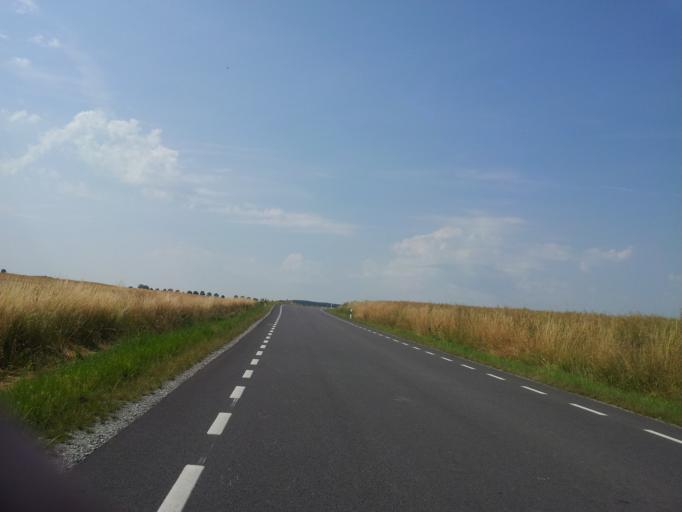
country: DE
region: Saxony
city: Panschwitz-Kuckau
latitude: 51.2283
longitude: 14.1883
